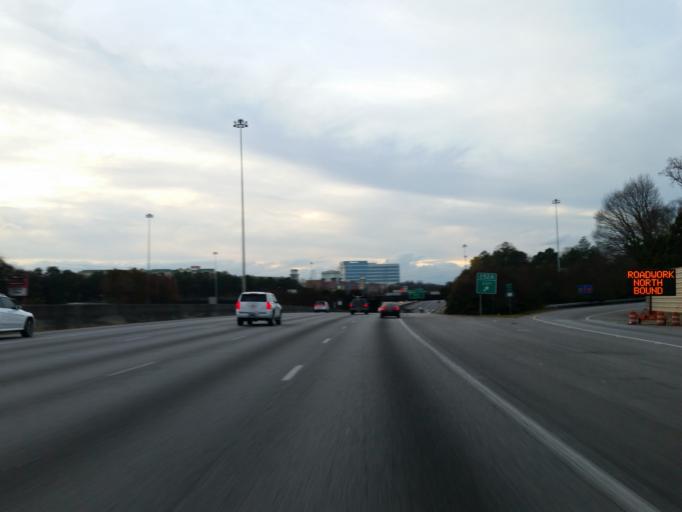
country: US
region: Georgia
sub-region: Fulton County
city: Atlanta
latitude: 33.8022
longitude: -84.4049
